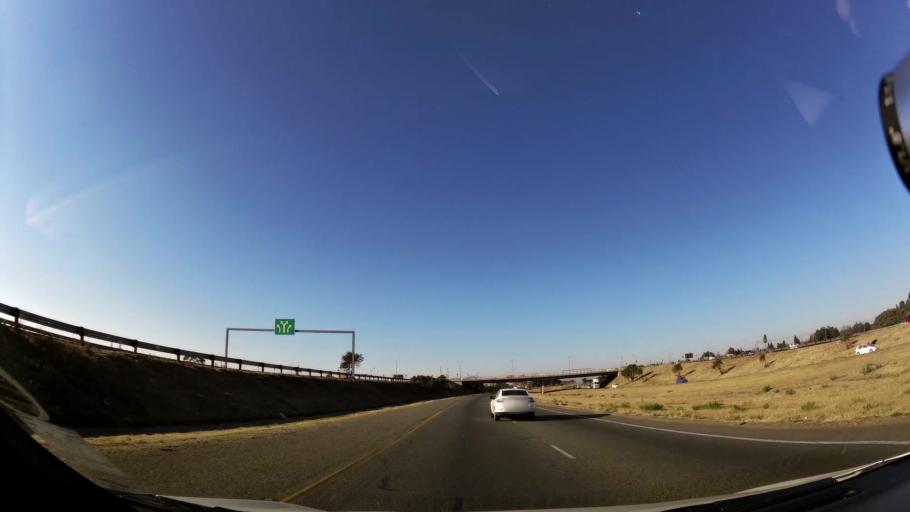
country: ZA
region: Gauteng
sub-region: Ekurhuleni Metropolitan Municipality
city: Germiston
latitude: -26.3039
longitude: 28.1115
